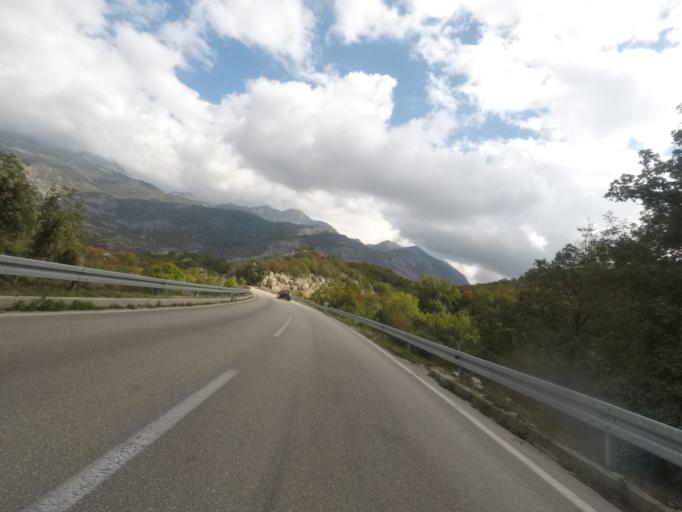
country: ME
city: Igalo
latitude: 42.5264
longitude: 18.4696
